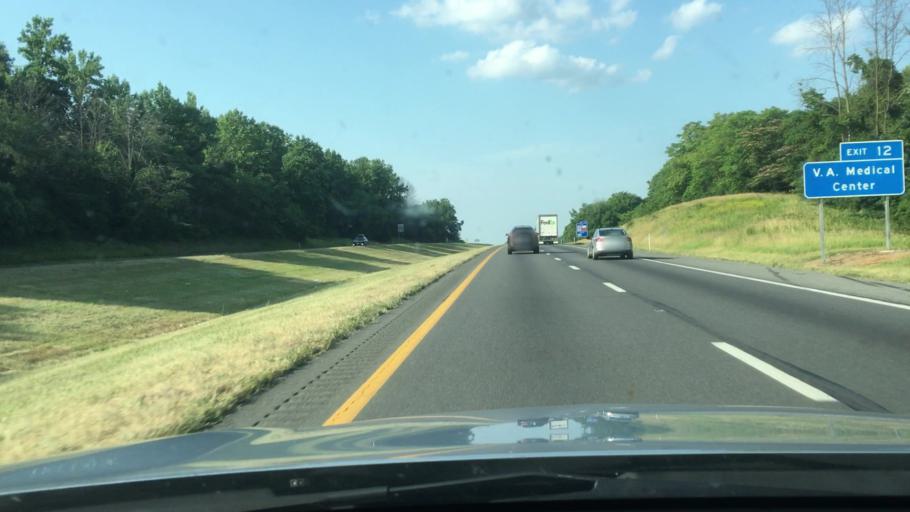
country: US
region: West Virginia
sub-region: Berkeley County
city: Martinsburg
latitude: 39.4325
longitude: -77.9949
